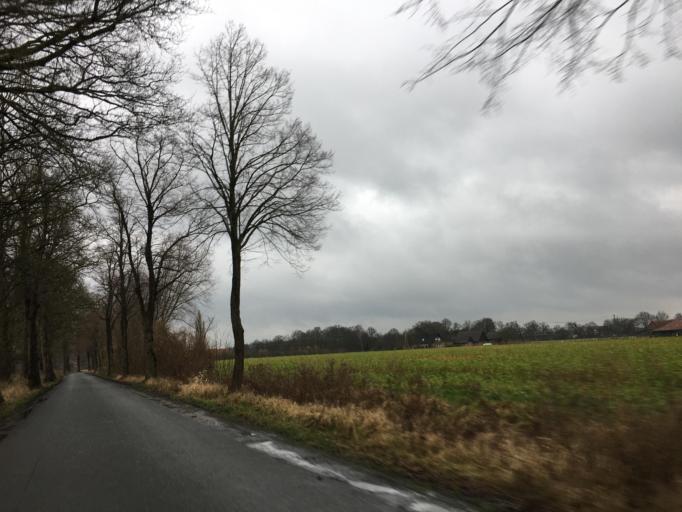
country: DE
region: North Rhine-Westphalia
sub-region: Regierungsbezirk Munster
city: Nordwalde
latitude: 52.0950
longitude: 7.5004
